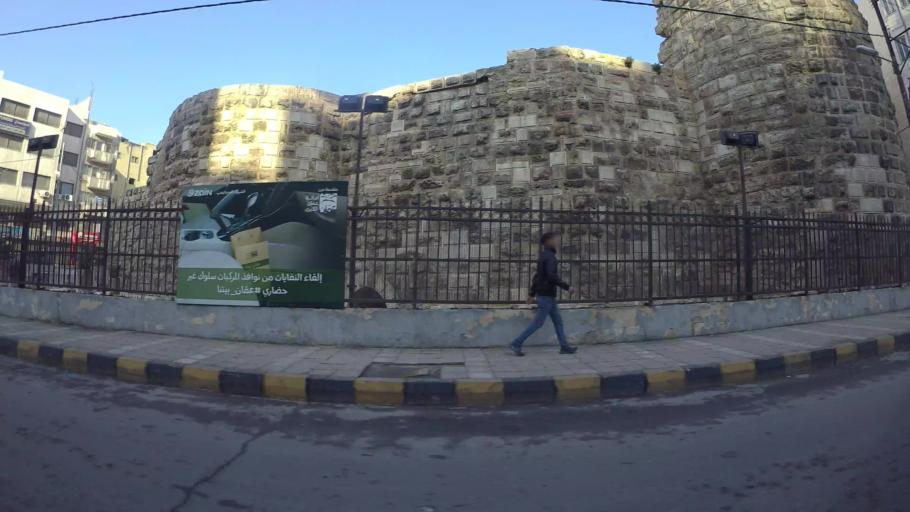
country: JO
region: Amman
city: Amman
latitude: 31.9503
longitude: 35.9365
